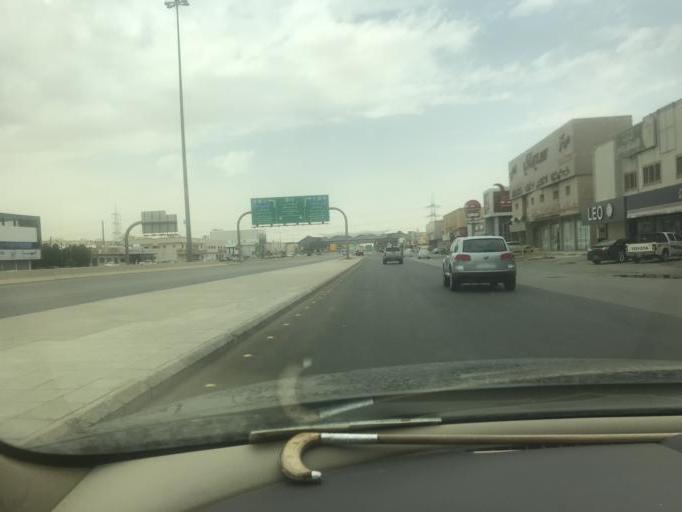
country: SA
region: Ar Riyad
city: Riyadh
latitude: 24.7959
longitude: 46.6992
